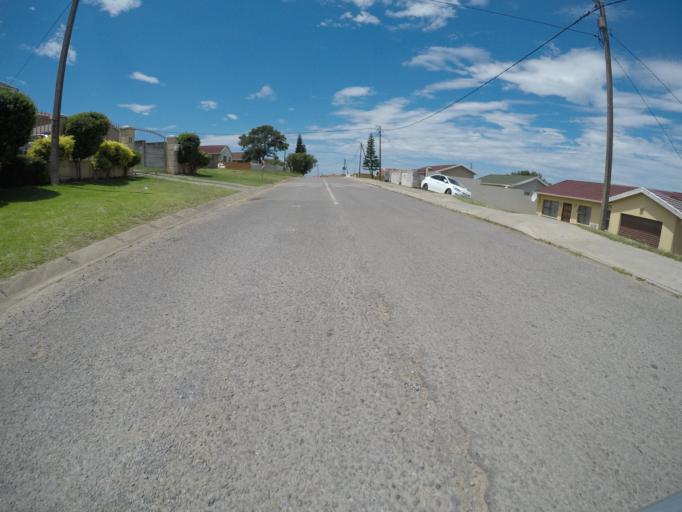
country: ZA
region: Eastern Cape
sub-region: Buffalo City Metropolitan Municipality
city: East London
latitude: -33.0423
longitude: 27.8626
